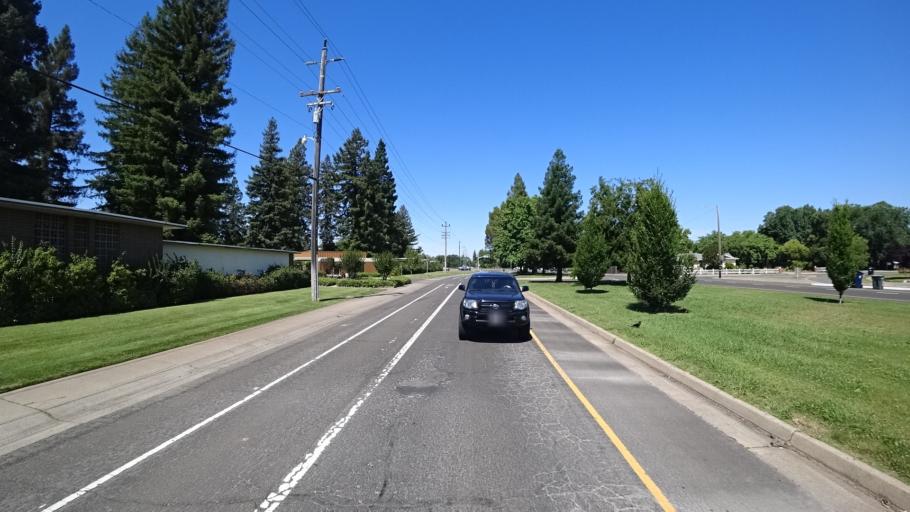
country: US
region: California
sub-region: Sacramento County
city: Florin
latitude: 38.5321
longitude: -121.4257
